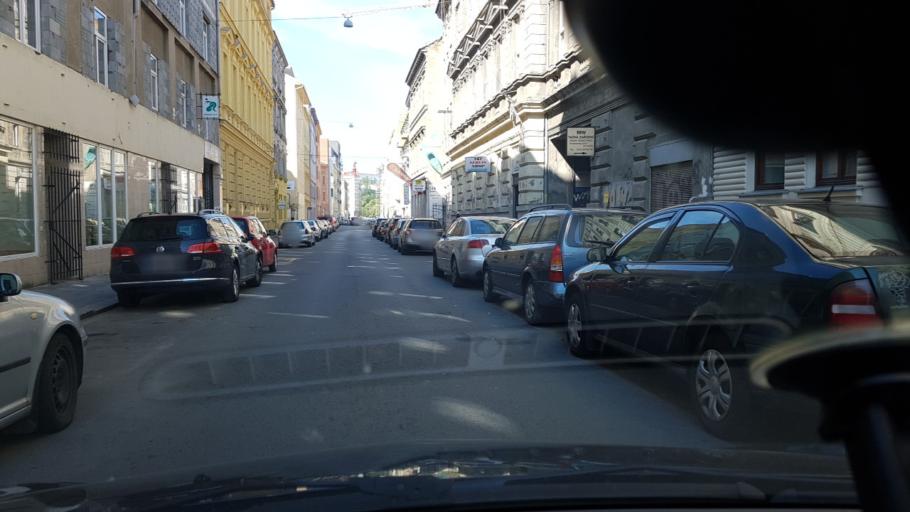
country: CZ
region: South Moravian
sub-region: Mesto Brno
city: Brno
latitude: 49.1997
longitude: 16.6203
